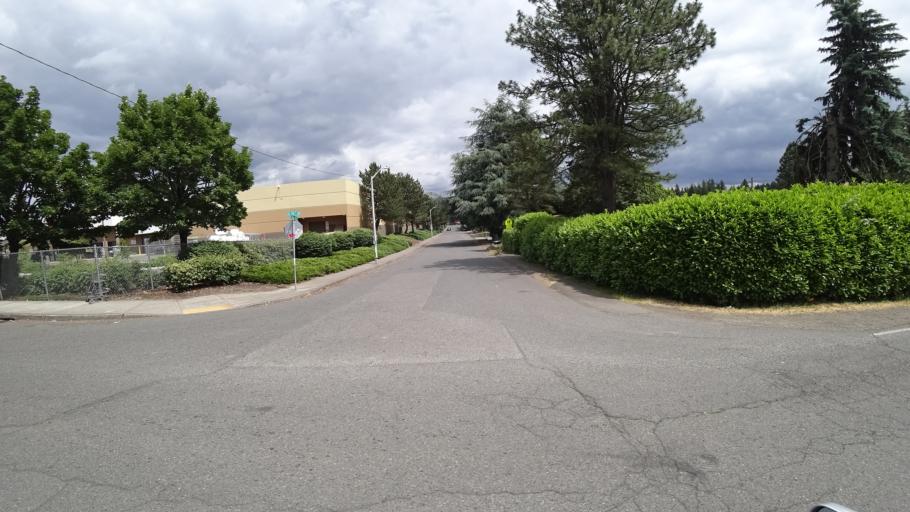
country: US
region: Oregon
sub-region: Multnomah County
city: Lents
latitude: 45.5025
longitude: -122.5139
